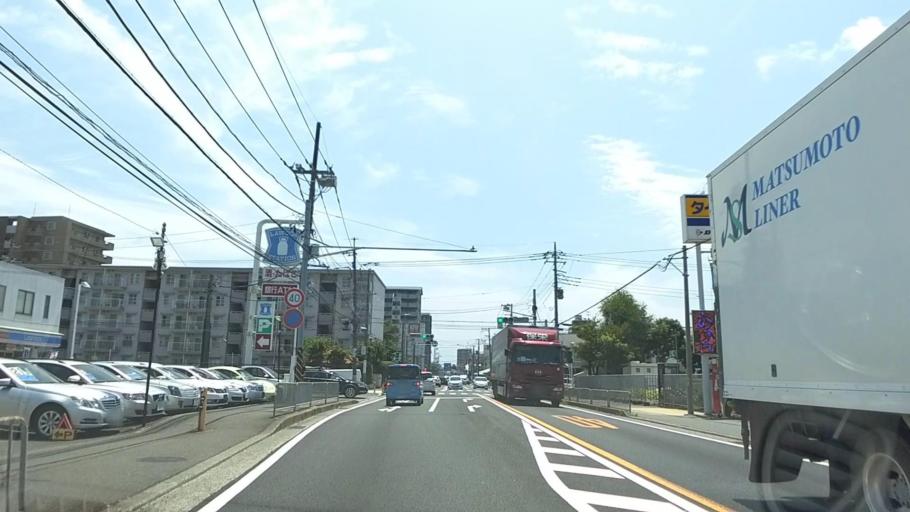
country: JP
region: Kanagawa
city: Atsugi
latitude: 35.4492
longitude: 139.3778
